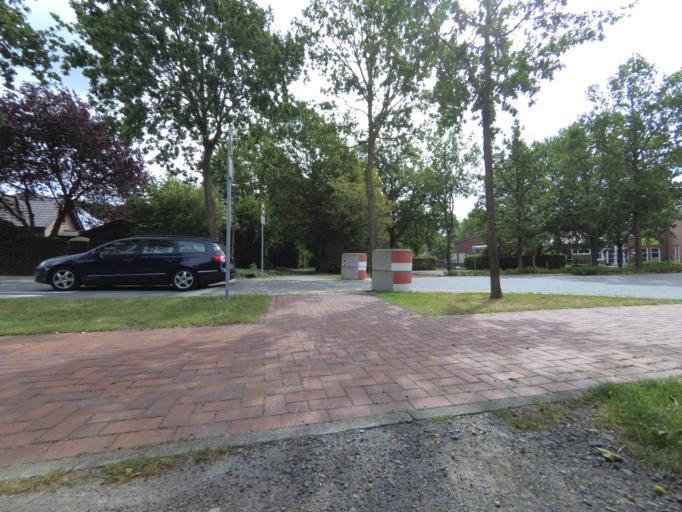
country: DE
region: North Rhine-Westphalia
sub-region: Regierungsbezirk Munster
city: Ahaus
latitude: 52.0803
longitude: 6.9883
